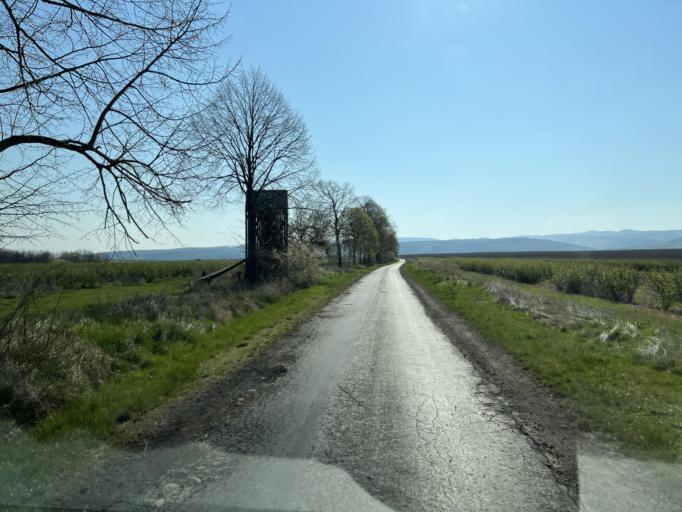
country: SK
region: Nitriansky
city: Sahy
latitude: 48.0456
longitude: 18.8803
